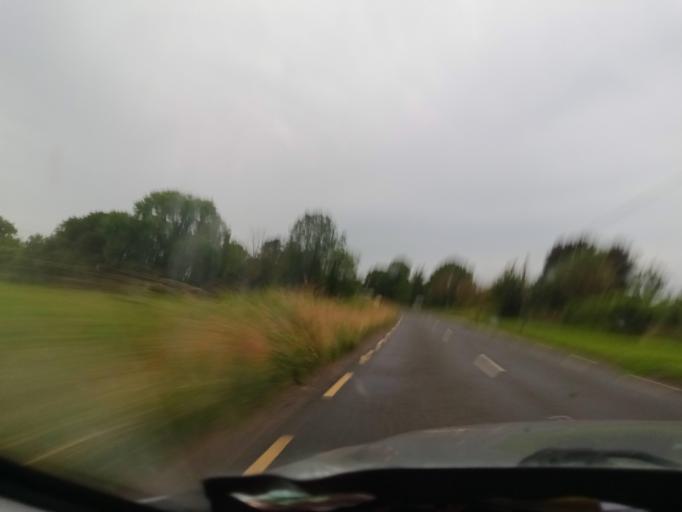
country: IE
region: Leinster
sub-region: Laois
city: Mountmellick
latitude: 53.1329
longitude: -7.3980
